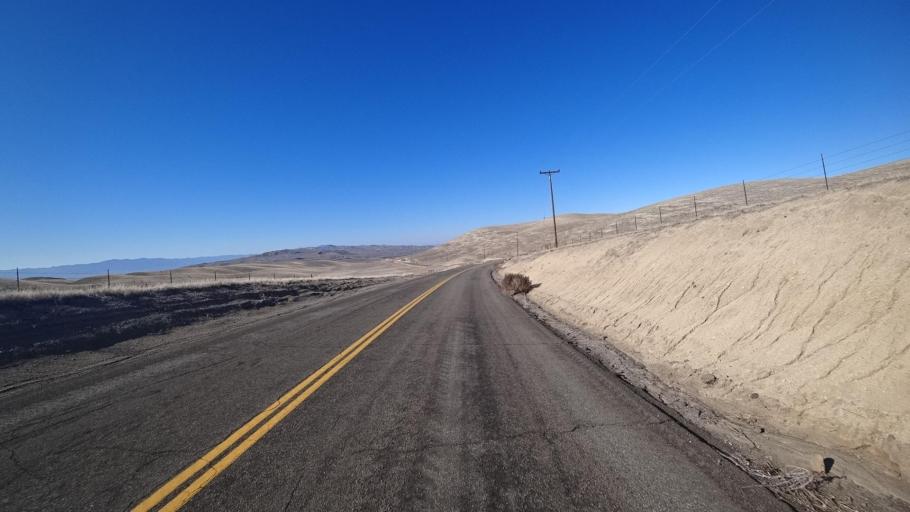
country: US
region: California
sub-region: Kern County
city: Maricopa
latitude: 34.9497
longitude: -119.4228
